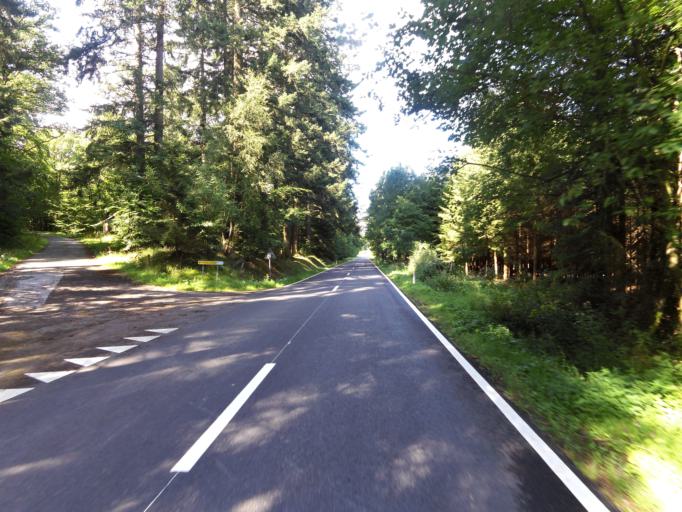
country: BE
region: Wallonia
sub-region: Province du Luxembourg
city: Nassogne
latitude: 50.1275
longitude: 5.3712
